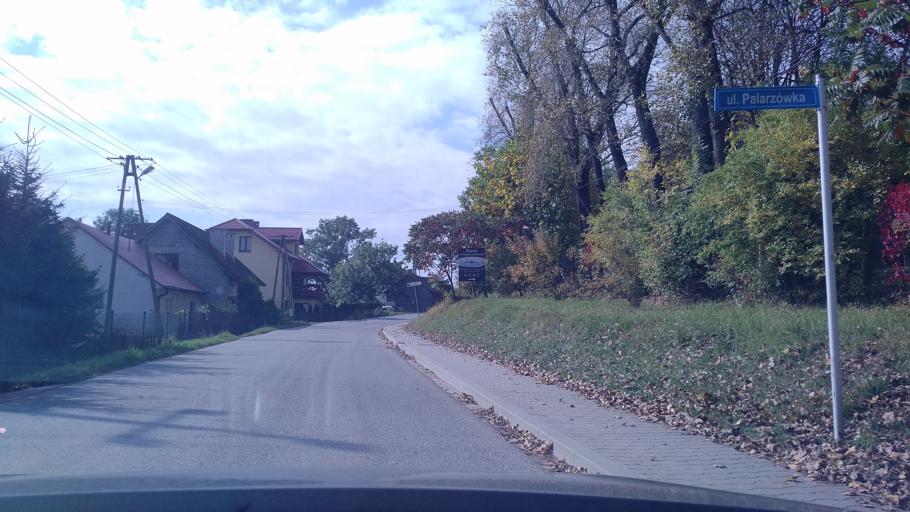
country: PL
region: Lesser Poland Voivodeship
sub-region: Powiat krakowski
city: Modlniczka
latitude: 50.1350
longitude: 19.8436
